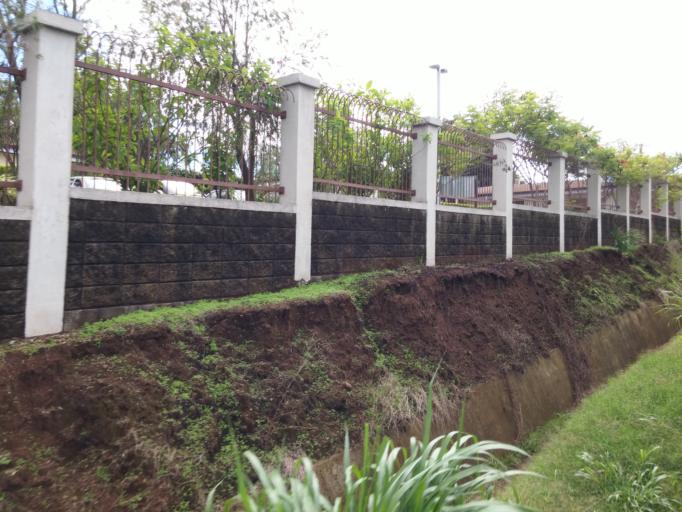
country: CR
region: Heredia
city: Mercedes
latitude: 9.9997
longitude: -84.1424
